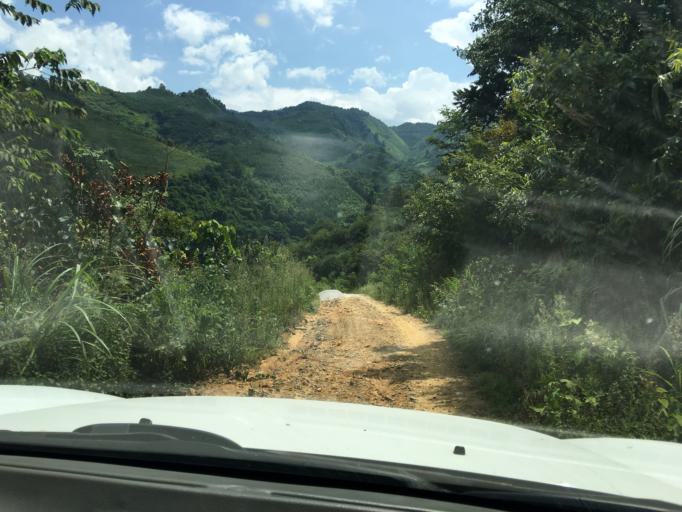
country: CN
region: Guangxi Zhuangzu Zizhiqu
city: Tongle
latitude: 24.9716
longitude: 105.9836
